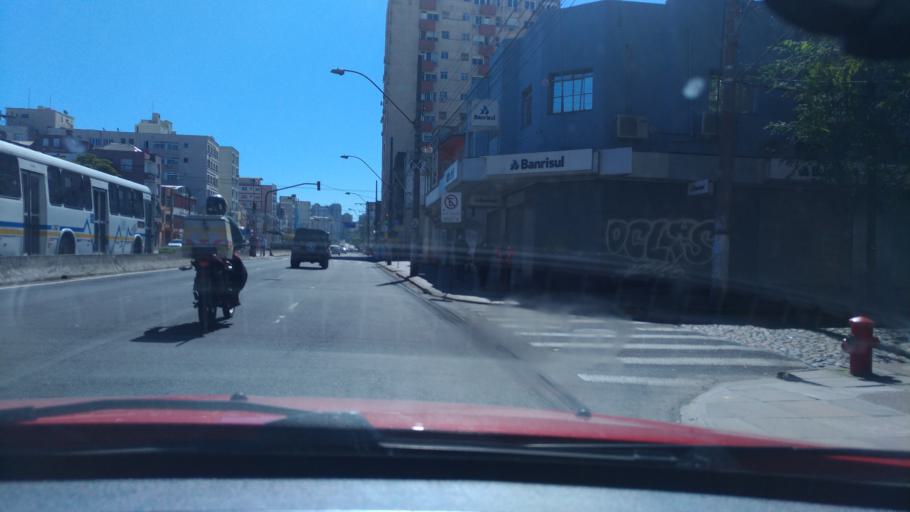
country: BR
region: Rio Grande do Sul
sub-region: Porto Alegre
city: Porto Alegre
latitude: -30.0428
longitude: -51.2150
